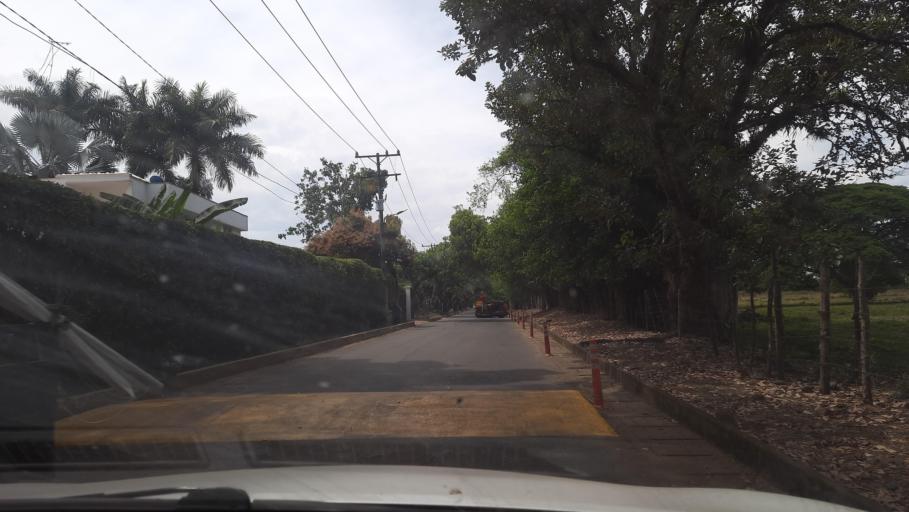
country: CO
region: Valle del Cauca
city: Jamundi
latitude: 3.2712
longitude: -76.5240
